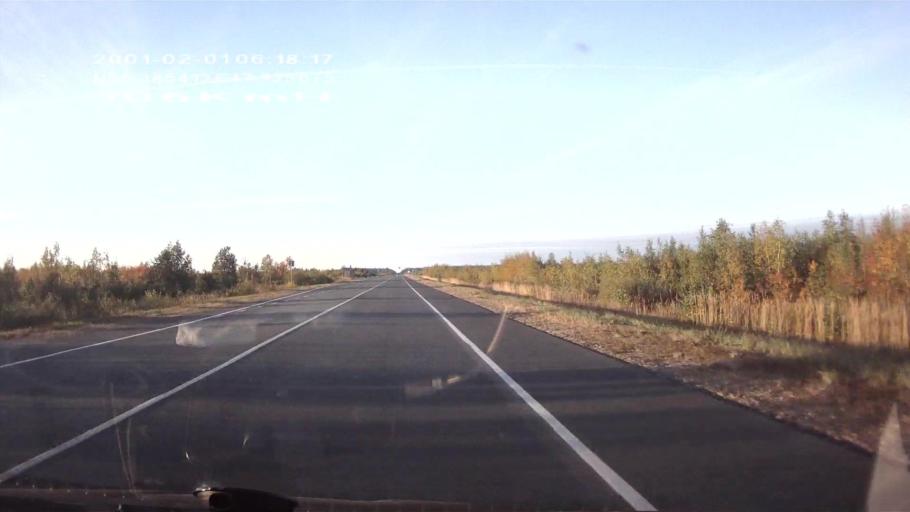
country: RU
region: Mariy-El
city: Medvedevo
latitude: 56.3849
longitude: 47.8256
